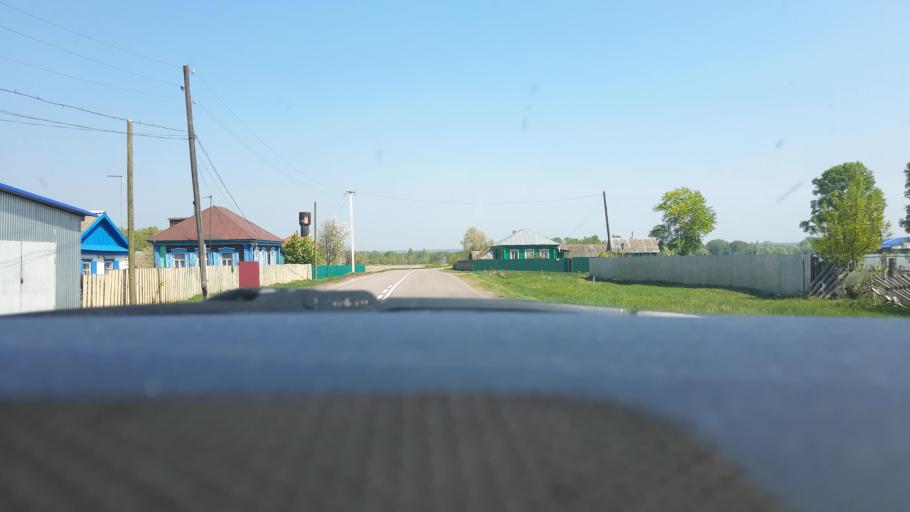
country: RU
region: Bashkortostan
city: Chishmy
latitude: 54.4497
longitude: 55.2591
